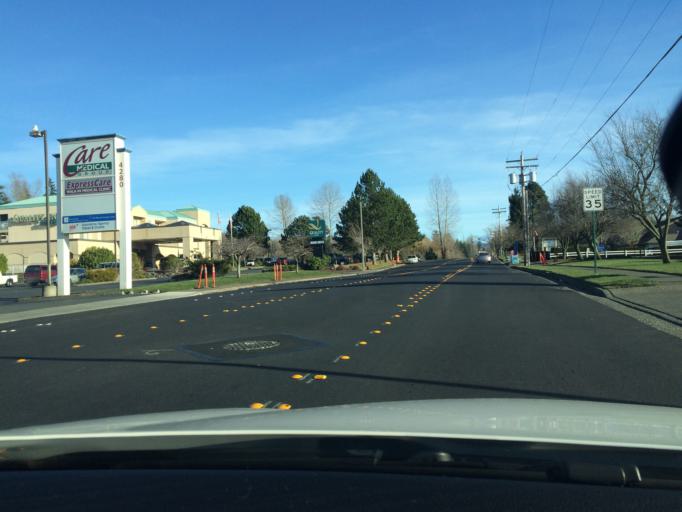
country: US
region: Washington
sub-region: Whatcom County
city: Bellingham
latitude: 48.7952
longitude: -122.4852
